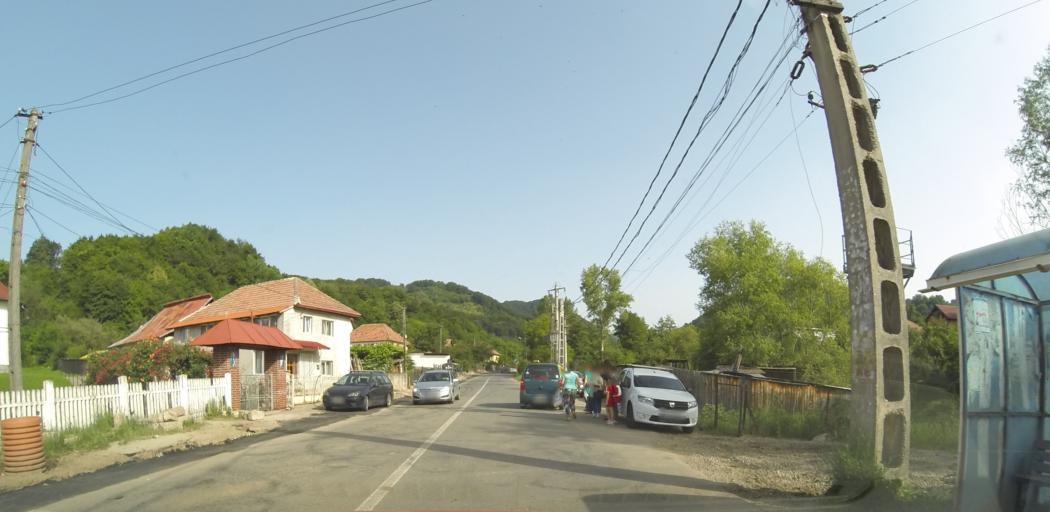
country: RO
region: Valcea
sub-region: Oras Baile Olanesti
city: Olanesti
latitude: 45.1831
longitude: 24.2562
